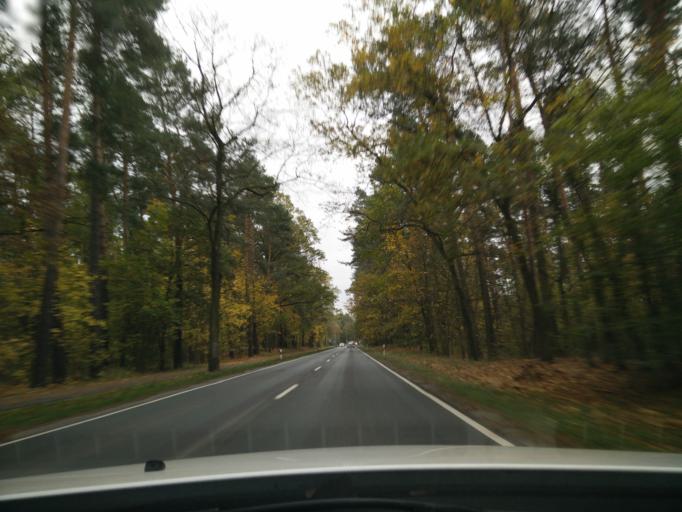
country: DE
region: Brandenburg
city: Falkensee
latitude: 52.5792
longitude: 13.1041
